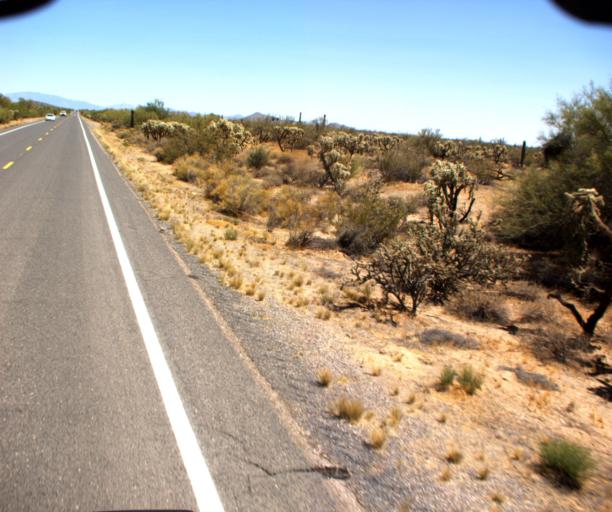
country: US
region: Arizona
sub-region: Pinal County
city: Florence
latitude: 32.8111
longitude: -111.1931
